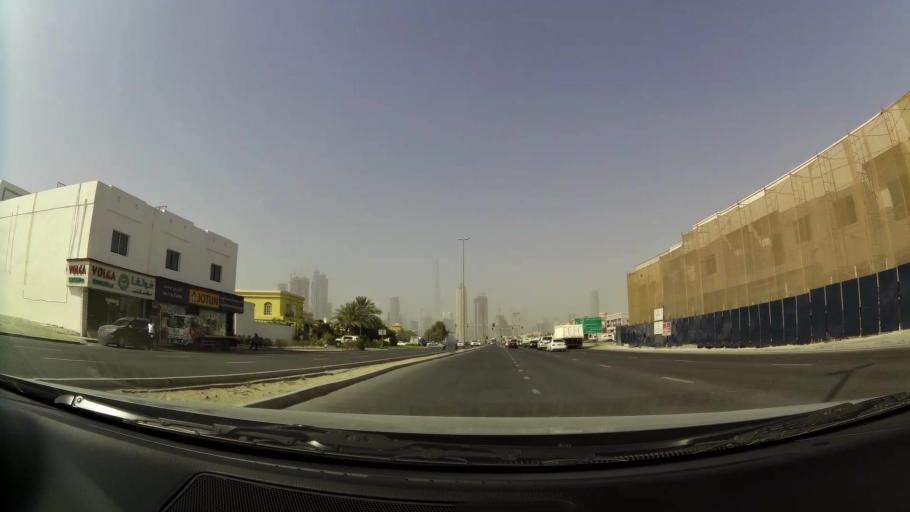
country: AE
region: Dubai
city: Dubai
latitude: 25.1685
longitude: 55.2505
